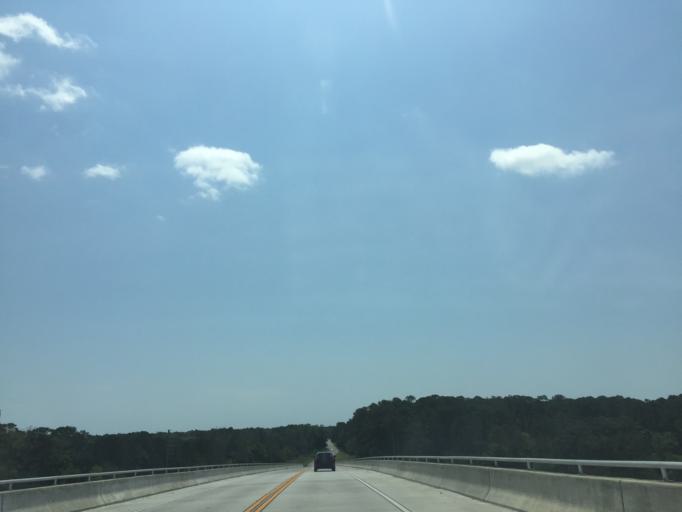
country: US
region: Georgia
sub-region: Chatham County
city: Skidaway Island
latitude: 31.9467
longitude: -81.0648
